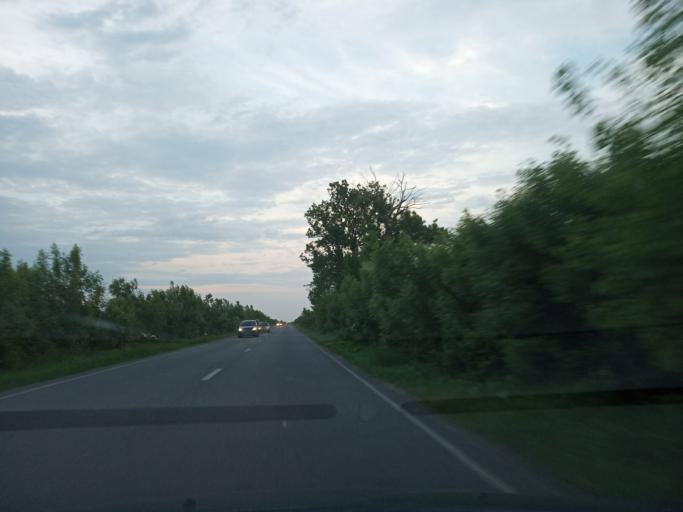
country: RO
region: Timis
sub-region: Comuna Voiteg
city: Voiteg
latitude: 45.4361
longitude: 21.2315
